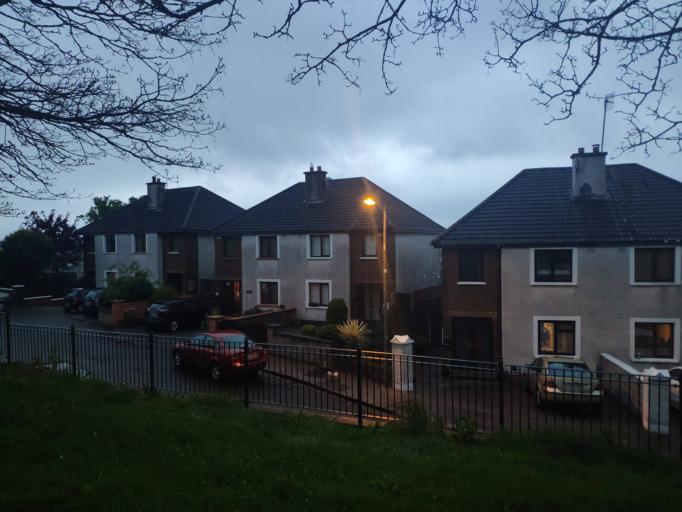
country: IE
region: Munster
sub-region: County Cork
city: Cork
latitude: 51.9103
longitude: -8.4570
